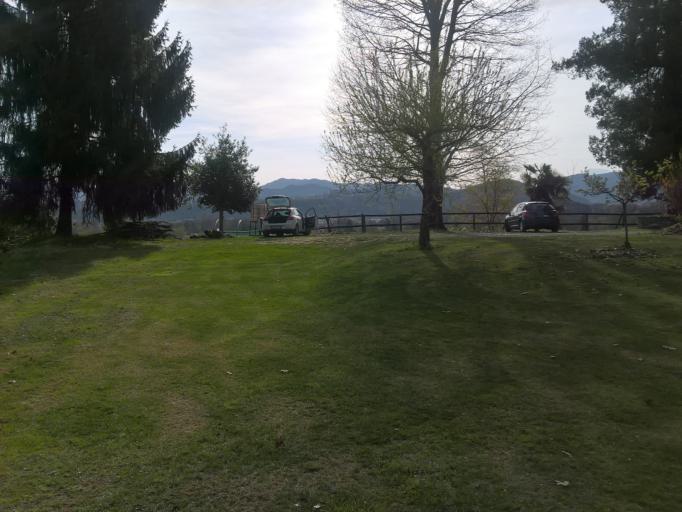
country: IT
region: Piedmont
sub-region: Provincia di Novara
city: Bolzano Novarese
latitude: 45.7605
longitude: 8.4423
